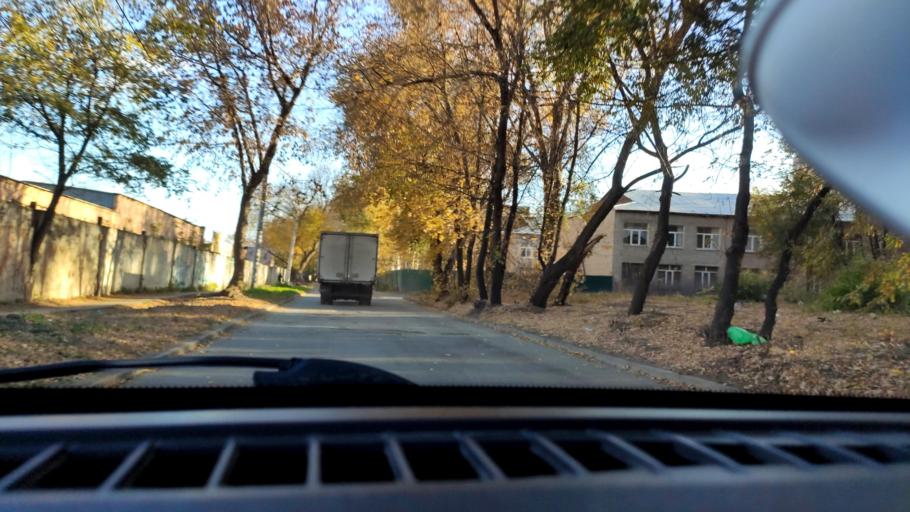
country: RU
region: Samara
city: Smyshlyayevka
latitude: 53.2189
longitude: 50.2737
